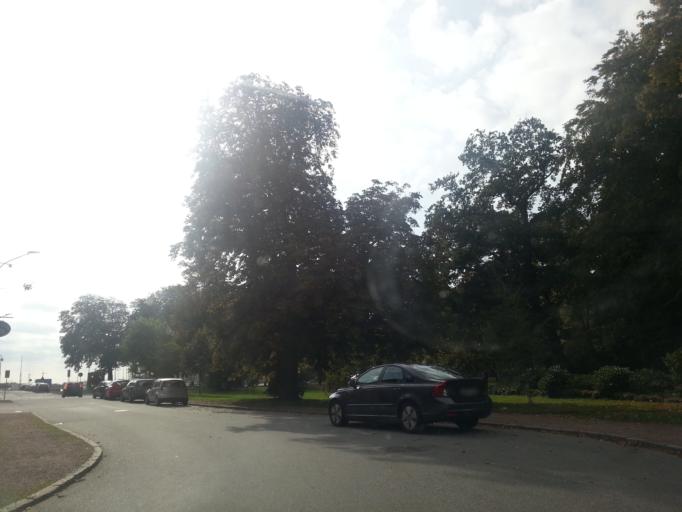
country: SE
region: Skane
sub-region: Landskrona
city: Landskrona
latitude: 55.8707
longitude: 12.8252
